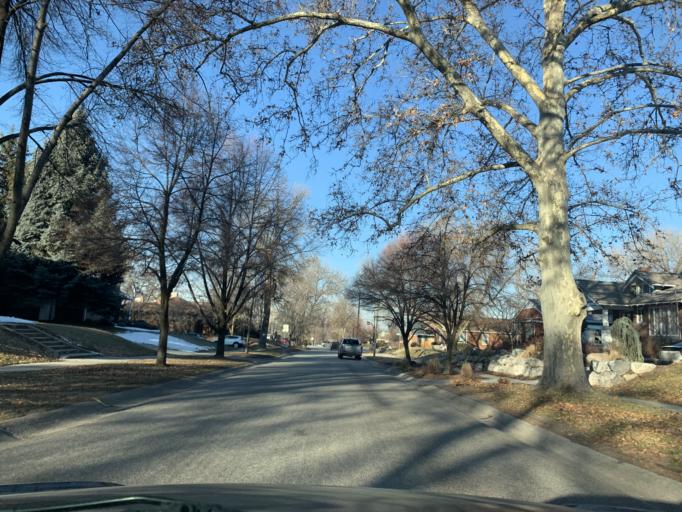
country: US
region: Utah
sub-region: Salt Lake County
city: Willard
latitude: 40.7155
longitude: -111.8517
